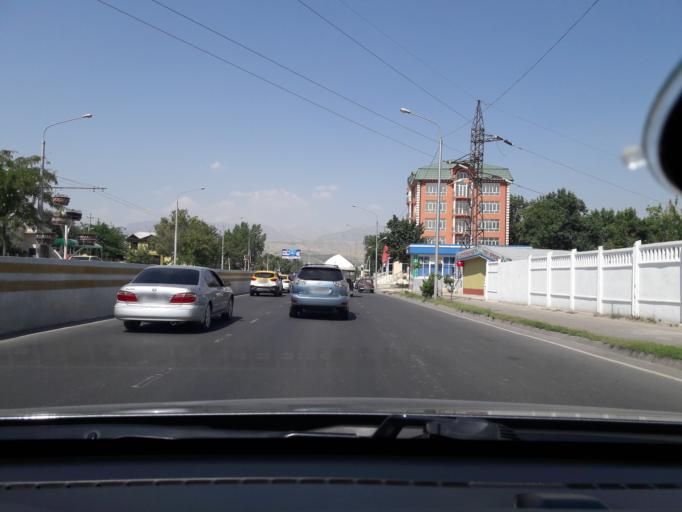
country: TJ
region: Dushanbe
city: Dushanbe
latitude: 38.5936
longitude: 68.7527
